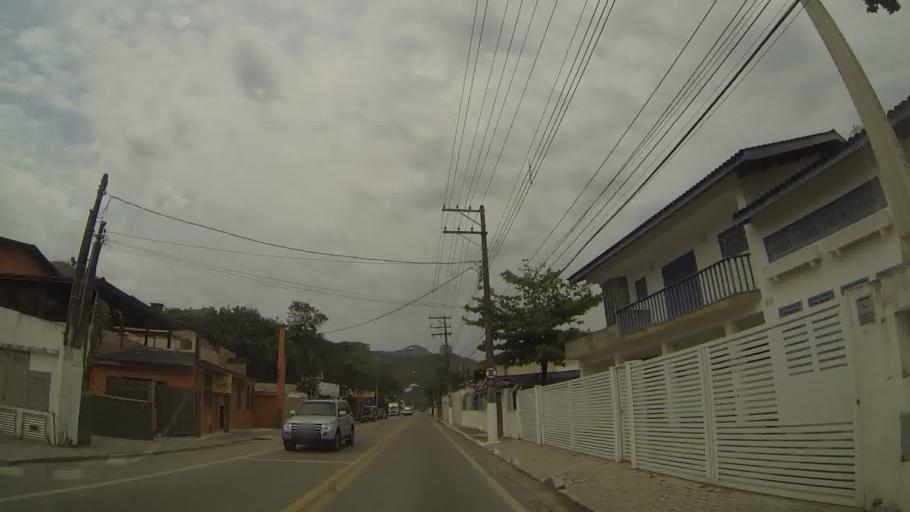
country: BR
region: Sao Paulo
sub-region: Sao Sebastiao
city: Sao Sebastiao
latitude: -23.7923
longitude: -45.5578
